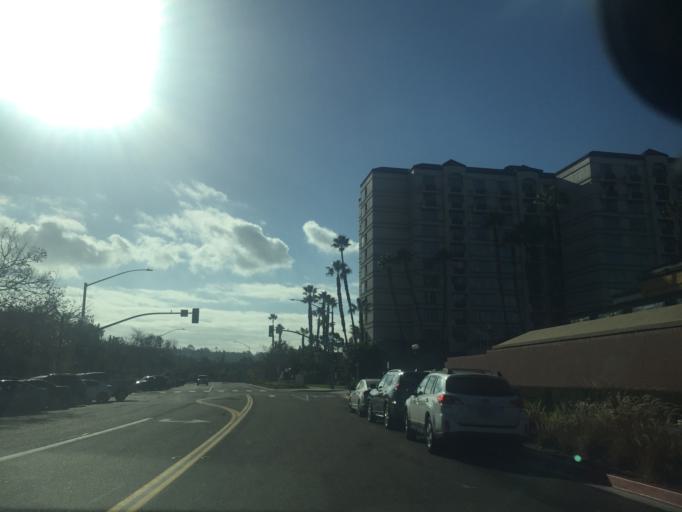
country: US
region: California
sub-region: San Diego County
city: San Diego
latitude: 32.7702
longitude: -117.1589
